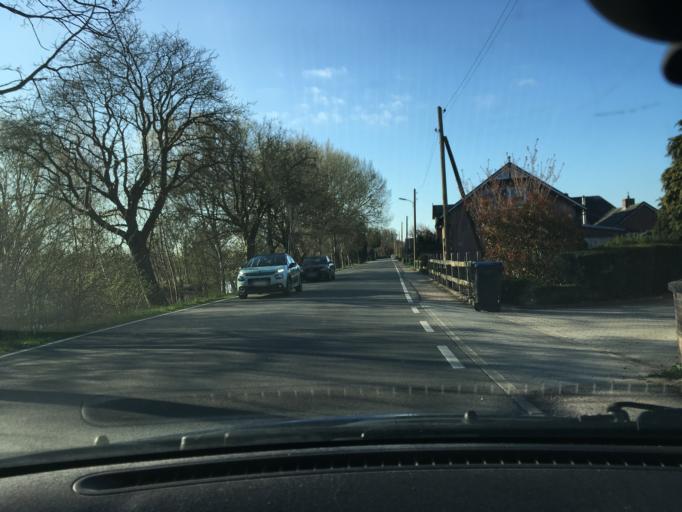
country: DE
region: Hamburg
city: Bergedorf
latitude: 53.4441
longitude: 10.2317
